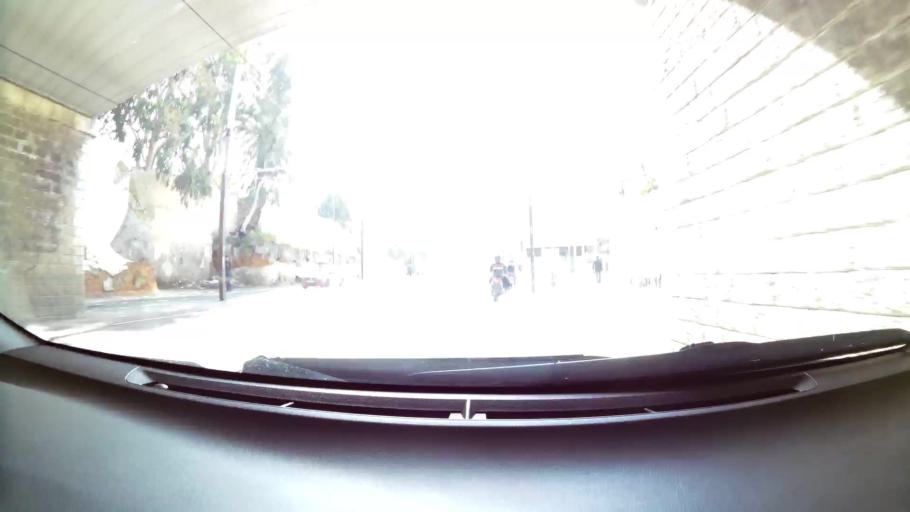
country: MA
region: Grand Casablanca
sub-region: Casablanca
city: Casablanca
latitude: 33.5946
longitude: -7.5846
